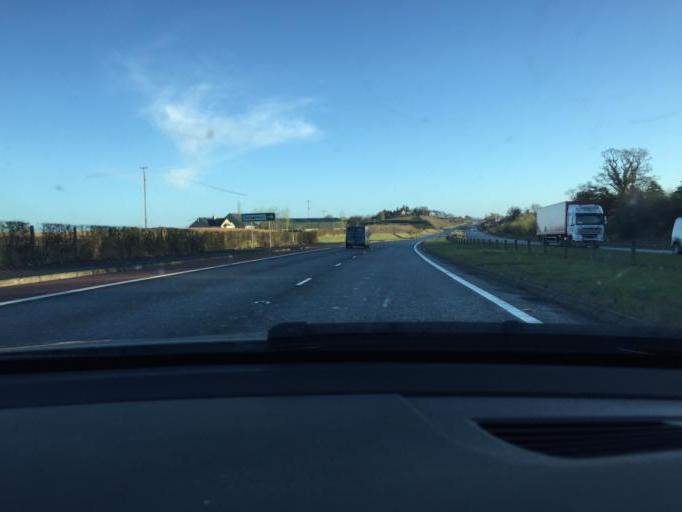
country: GB
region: Northern Ireland
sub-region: Newry and Mourne District
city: Newry
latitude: 54.2463
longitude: -6.3224
